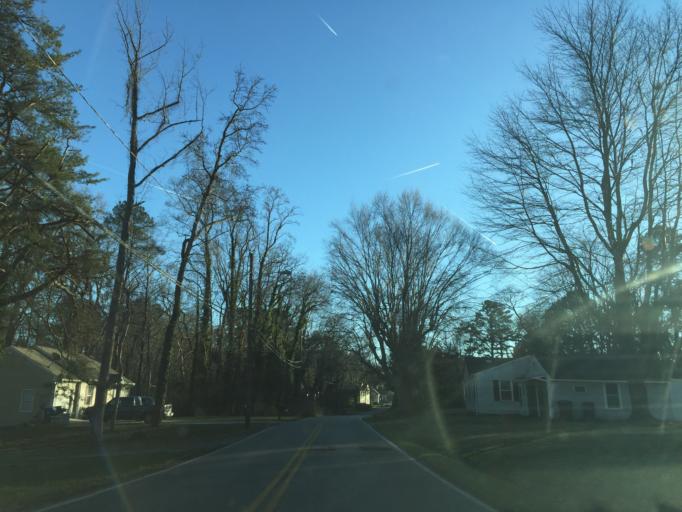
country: US
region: Virginia
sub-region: City of Newport News
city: Newport News
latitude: 37.0804
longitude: -76.5141
